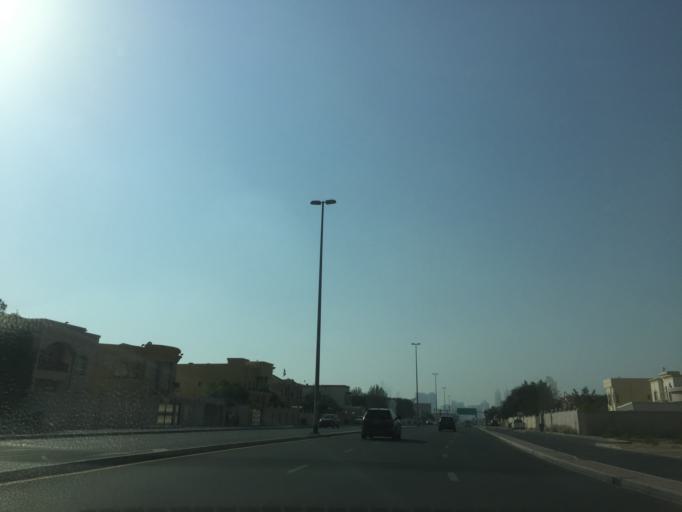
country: AE
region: Dubai
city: Dubai
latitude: 25.1006
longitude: 55.2116
